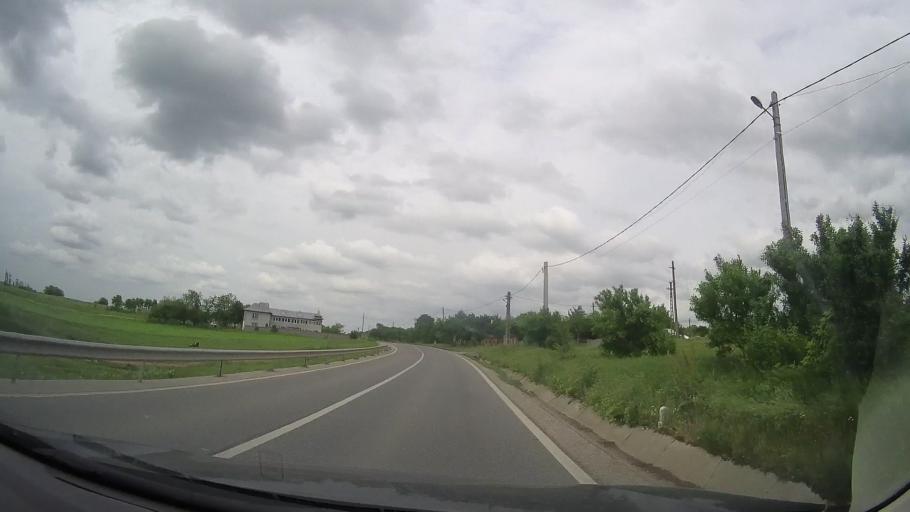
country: RO
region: Dolj
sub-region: Comuna Diosti
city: Radomir
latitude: 44.1242
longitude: 24.1579
